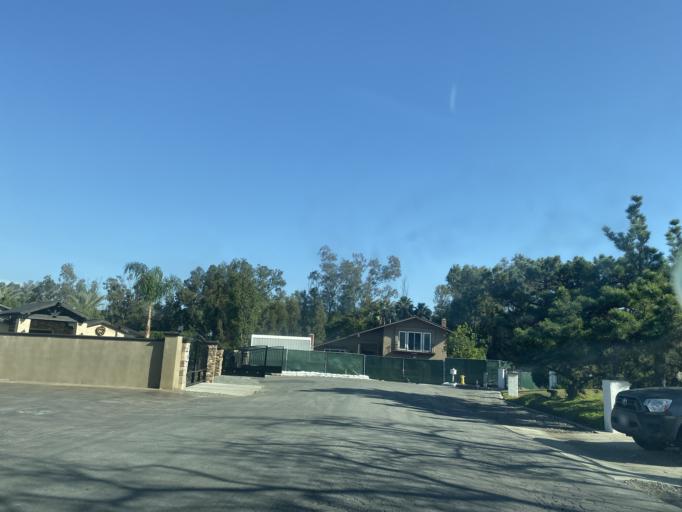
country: US
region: California
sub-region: Orange County
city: Villa Park
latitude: 33.8040
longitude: -117.7797
